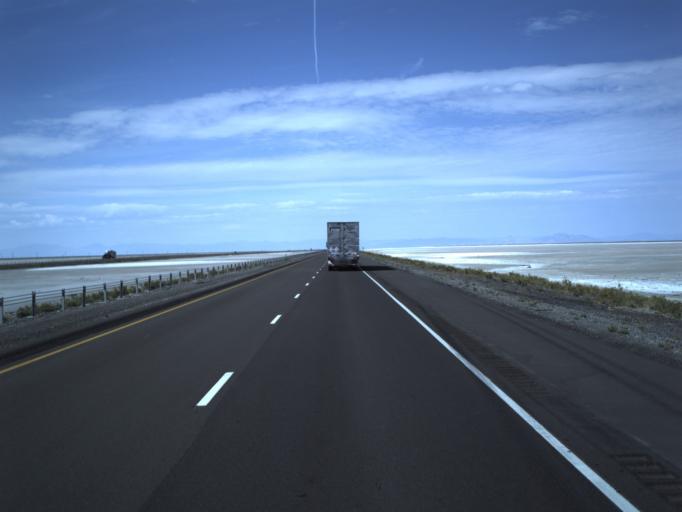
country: US
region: Utah
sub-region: Tooele County
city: Wendover
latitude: 40.7289
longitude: -113.3742
